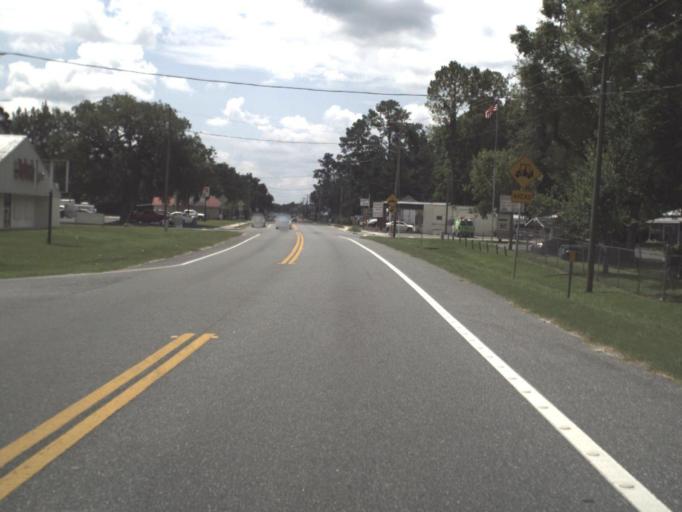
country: US
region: Florida
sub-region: Lafayette County
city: Mayo
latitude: 29.9653
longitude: -82.9320
